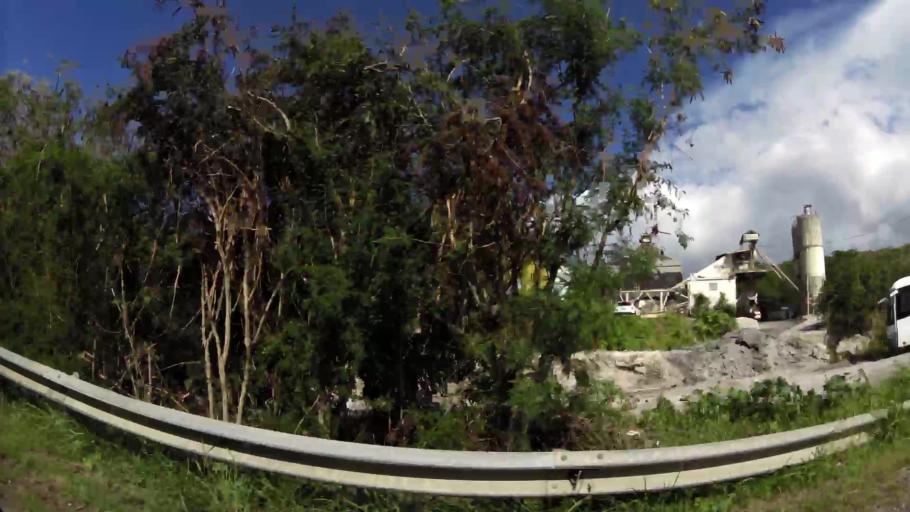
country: GP
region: Guadeloupe
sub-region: Guadeloupe
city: Baillif
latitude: 16.0326
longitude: -61.7479
